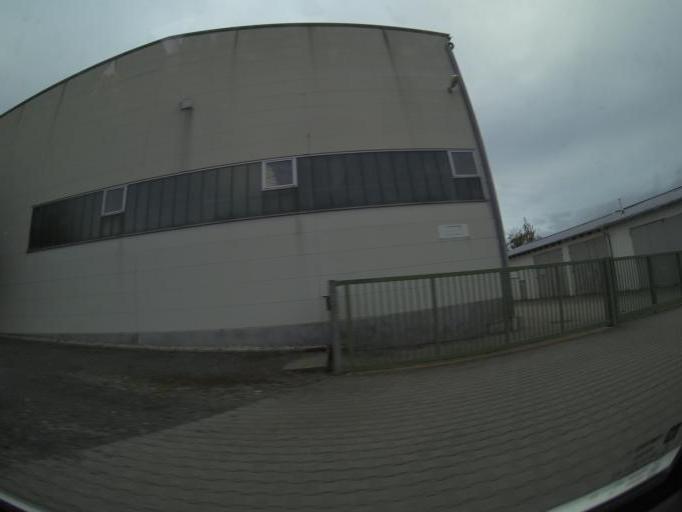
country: DE
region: Thuringia
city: Nobdenitz
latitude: 50.8802
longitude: 12.2795
